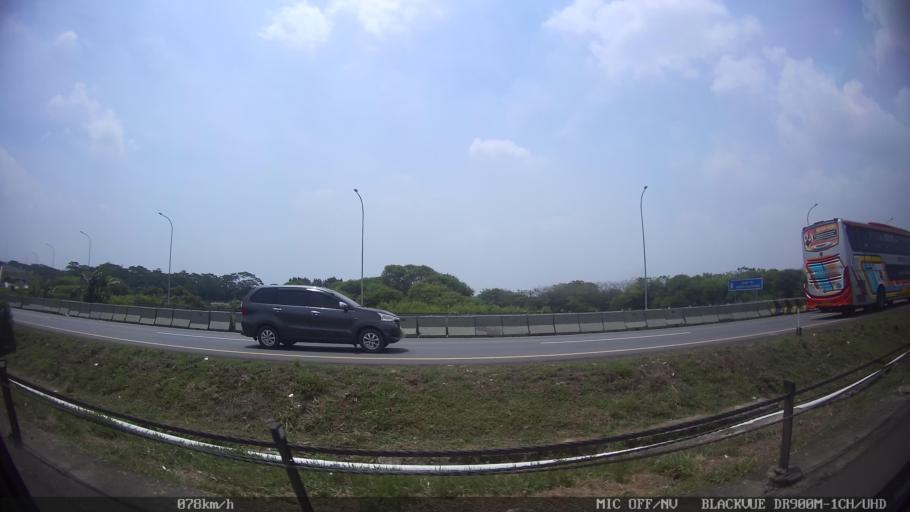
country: ID
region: Banten
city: Serang
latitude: -6.1390
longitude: 106.2496
